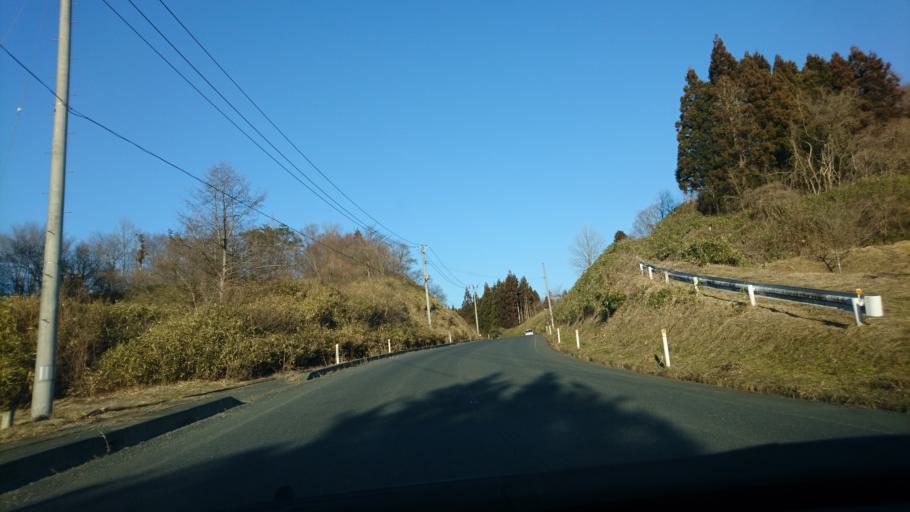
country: JP
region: Iwate
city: Ichinoseki
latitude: 38.9466
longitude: 141.3617
